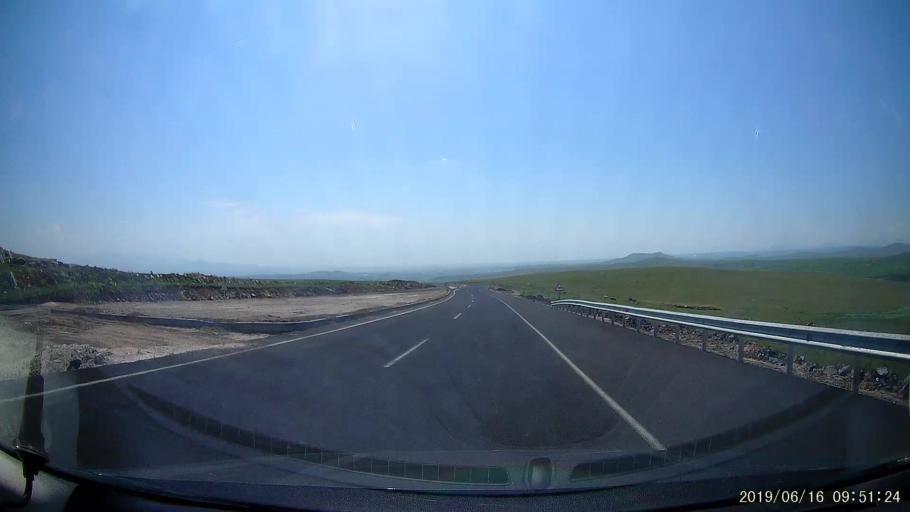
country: TR
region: Kars
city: Digor
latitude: 40.3914
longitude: 43.3668
